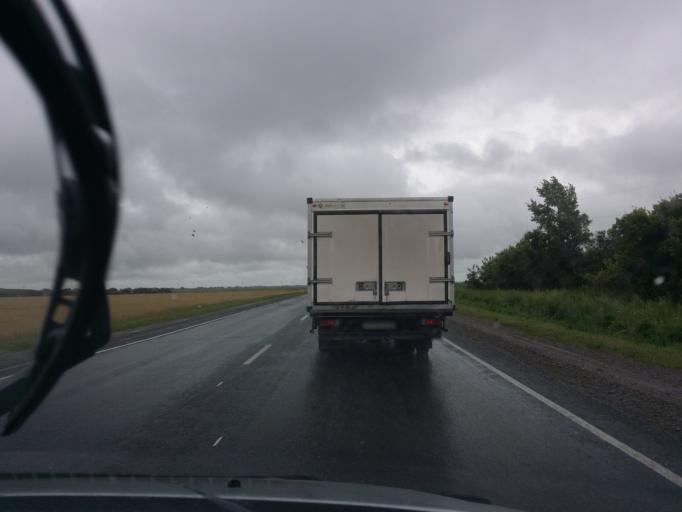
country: RU
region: Altai Krai
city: Zonal'noye
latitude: 52.7309
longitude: 84.9634
